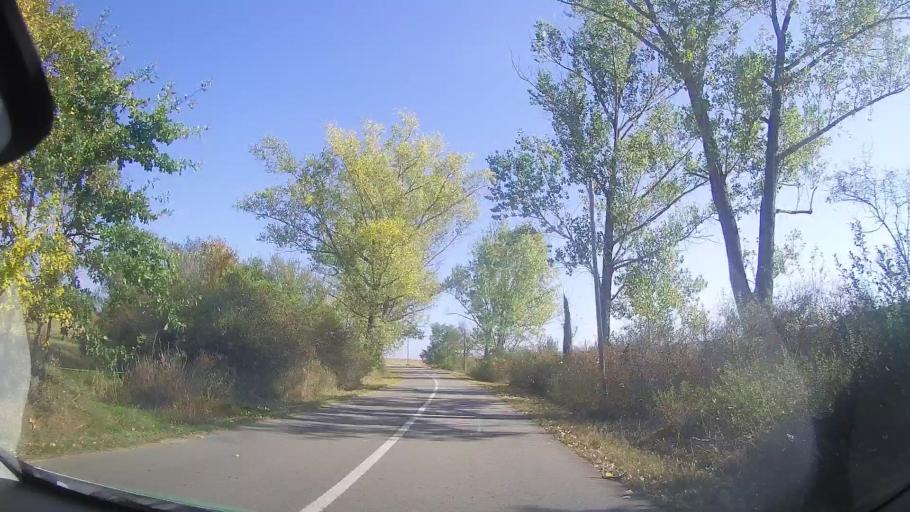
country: RO
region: Timis
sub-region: Comuna Secas
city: Secas
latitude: 45.8563
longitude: 21.8011
